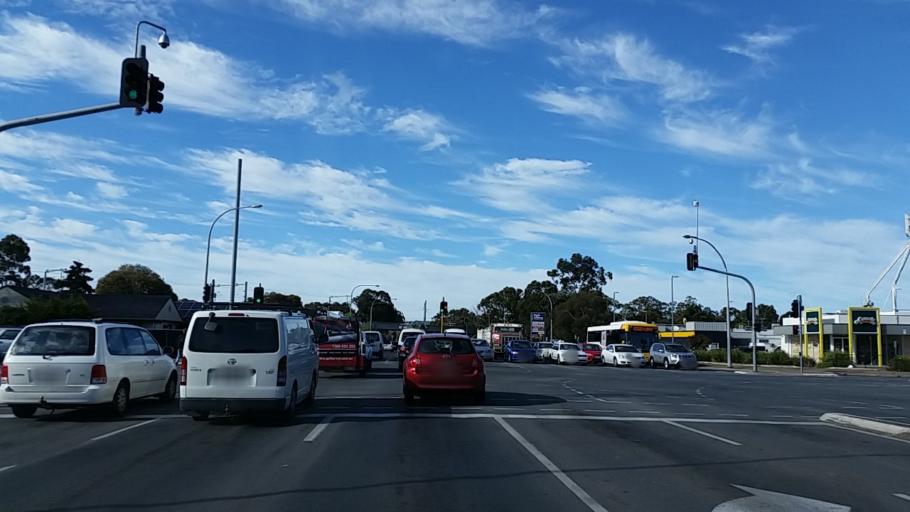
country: AU
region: South Australia
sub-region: Marion
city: Clovelly Park
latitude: -34.9934
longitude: 138.5570
